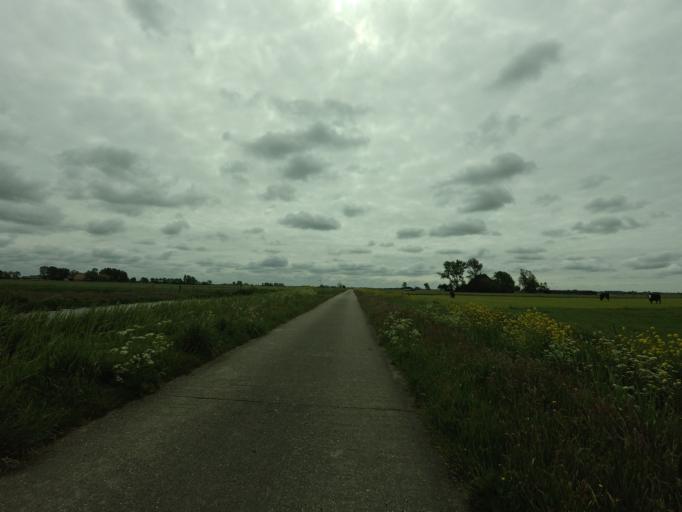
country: NL
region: Friesland
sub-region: Sudwest Fryslan
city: Workum
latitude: 52.9488
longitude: 5.4555
